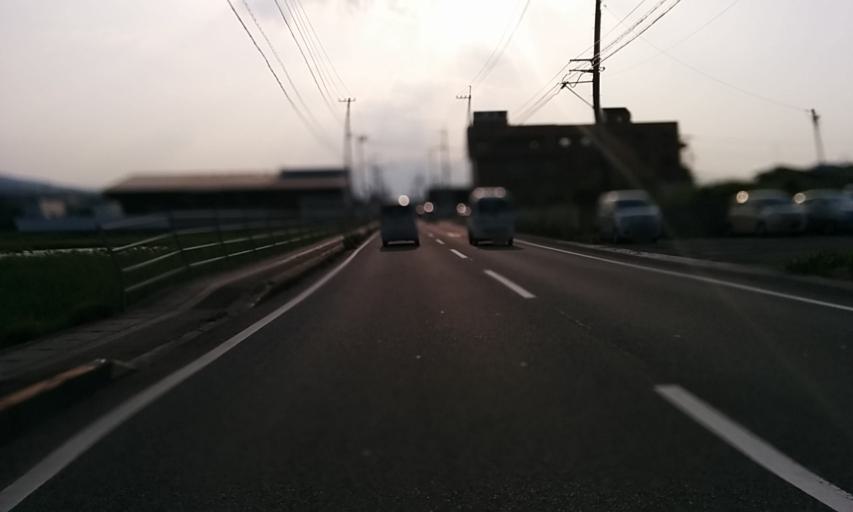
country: JP
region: Ehime
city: Saijo
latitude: 33.8947
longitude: 133.1551
